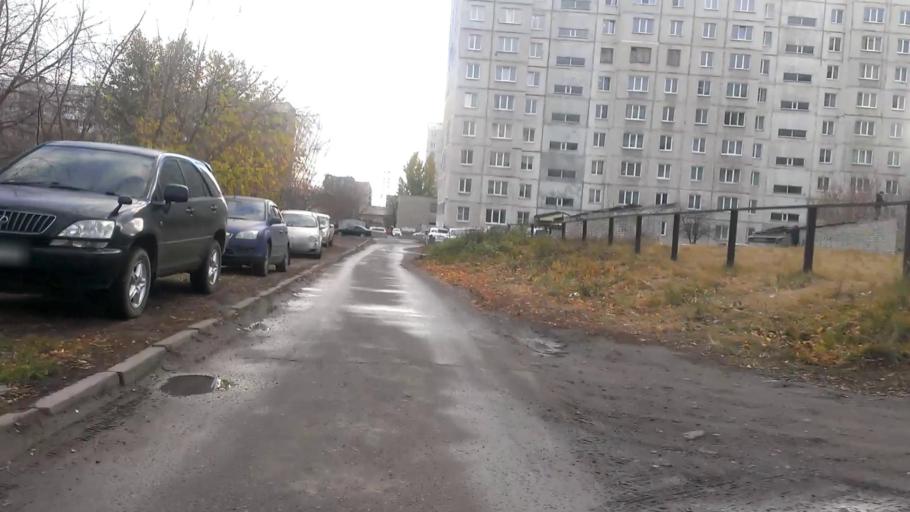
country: RU
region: Altai Krai
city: Novosilikatnyy
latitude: 53.3582
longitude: 83.6762
